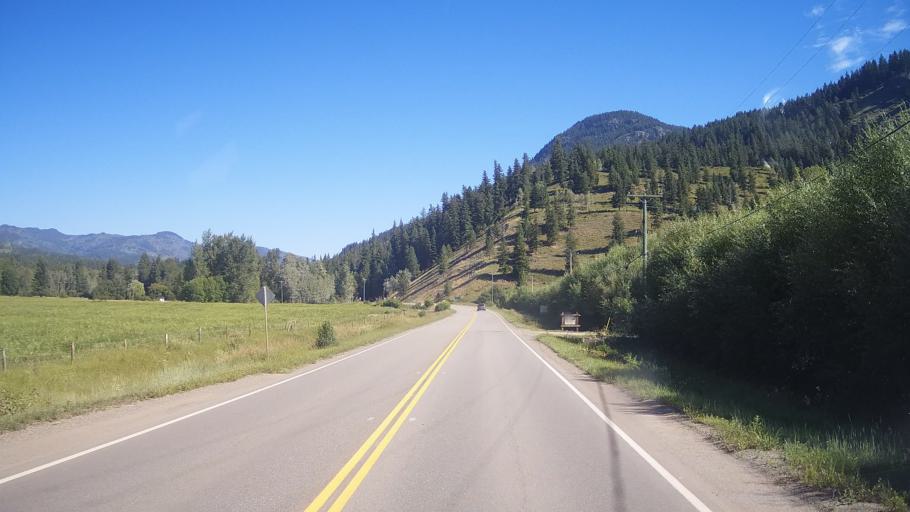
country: CA
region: British Columbia
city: Kamloops
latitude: 51.4332
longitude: -120.2078
